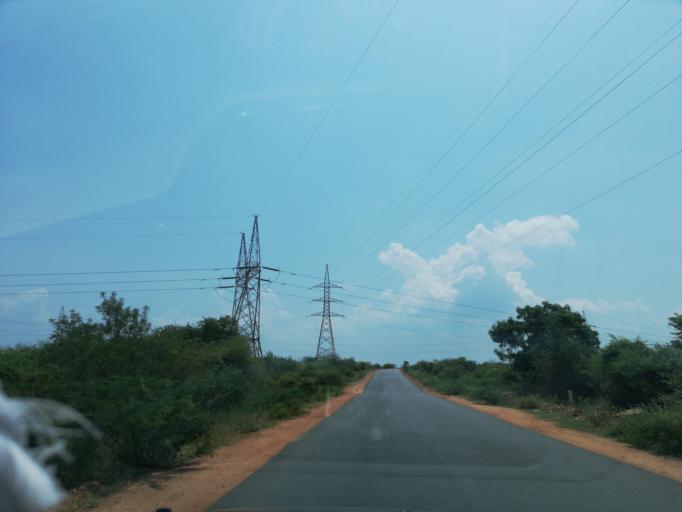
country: IN
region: Andhra Pradesh
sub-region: Guntur
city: Macherla
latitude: 16.5682
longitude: 79.3452
